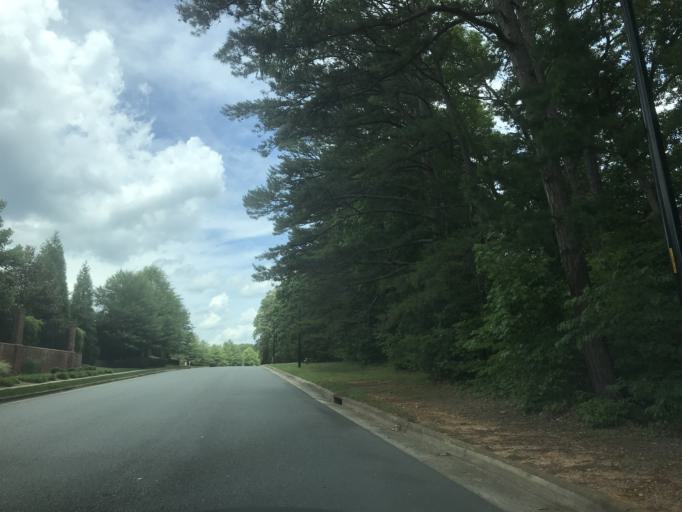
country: US
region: North Carolina
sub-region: Wake County
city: West Raleigh
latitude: 35.8986
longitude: -78.6586
